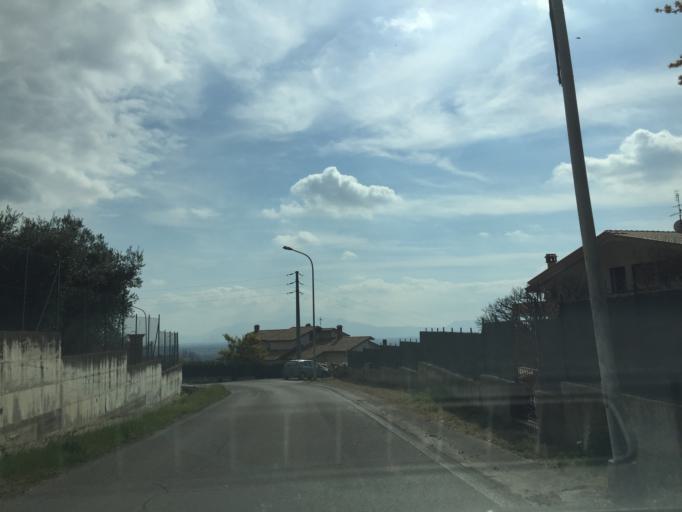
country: IT
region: Latium
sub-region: Provincia di Frosinone
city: Castrocielo
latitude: 41.5274
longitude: 13.7003
